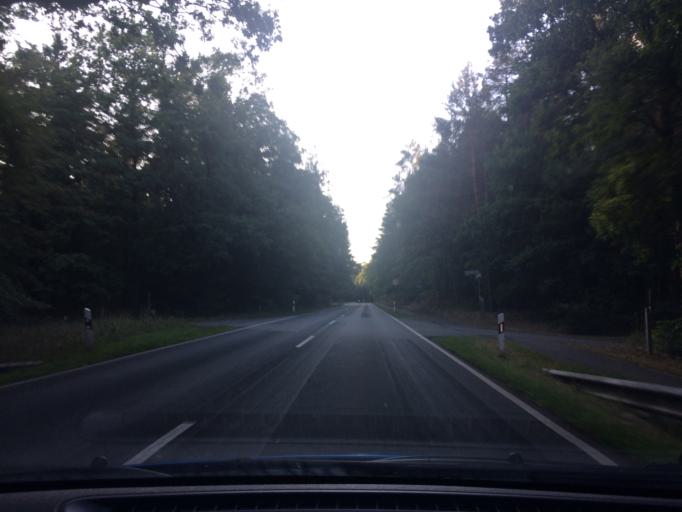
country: DE
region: Lower Saxony
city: Unterluss
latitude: 52.7993
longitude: 10.3796
